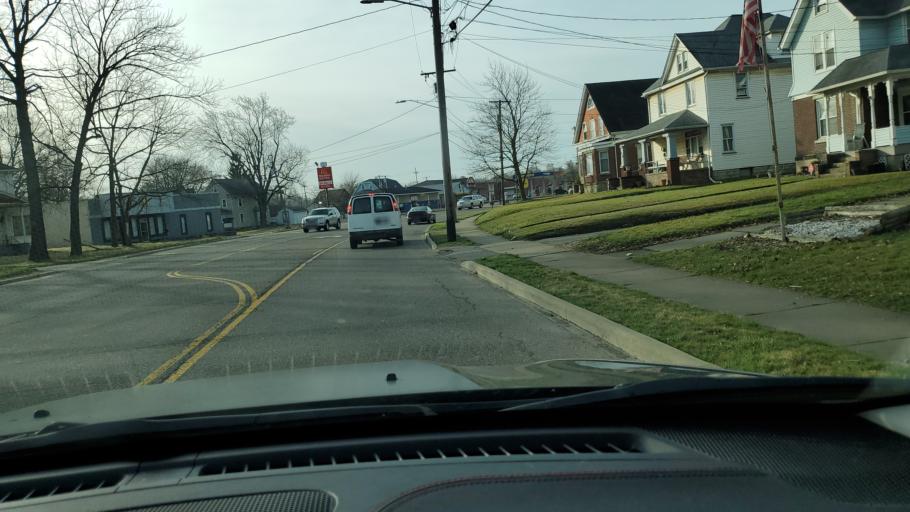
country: US
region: Ohio
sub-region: Trumbull County
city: Niles
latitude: 41.1879
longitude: -80.7655
